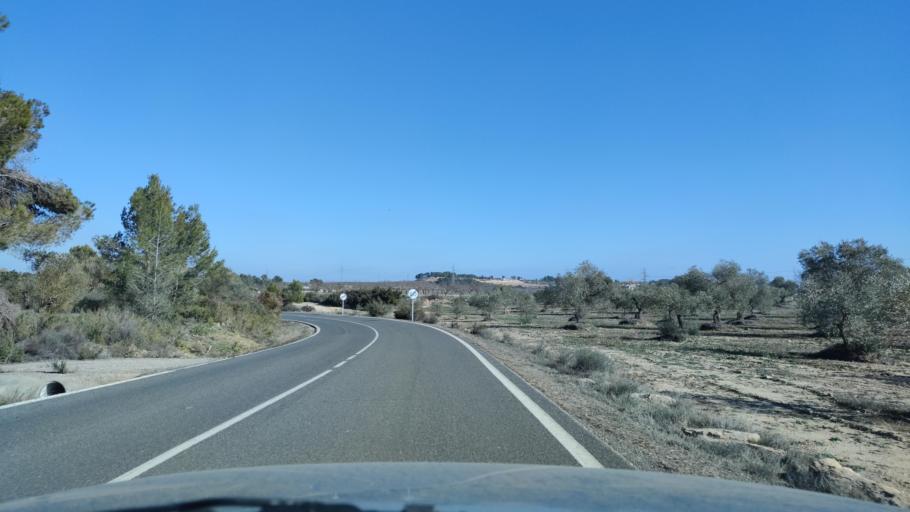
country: ES
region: Catalonia
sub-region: Provincia de Lleida
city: Maials
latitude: 41.3387
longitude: 0.4619
